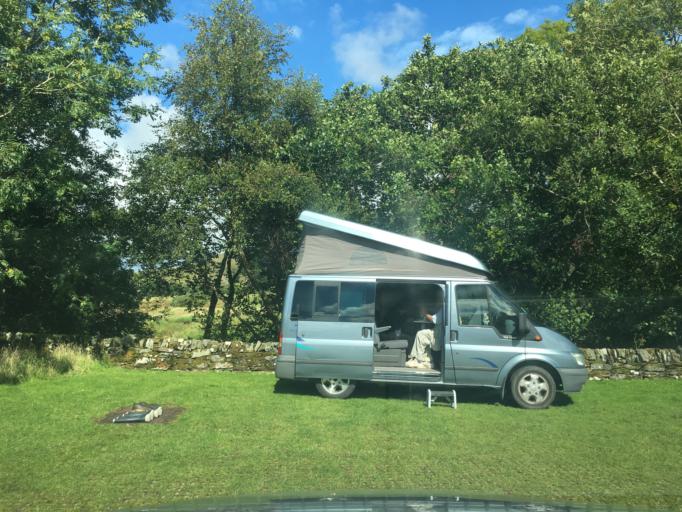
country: GB
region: Scotland
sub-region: Argyll and Bute
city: Lochgilphead
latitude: 56.0855
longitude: -5.4753
